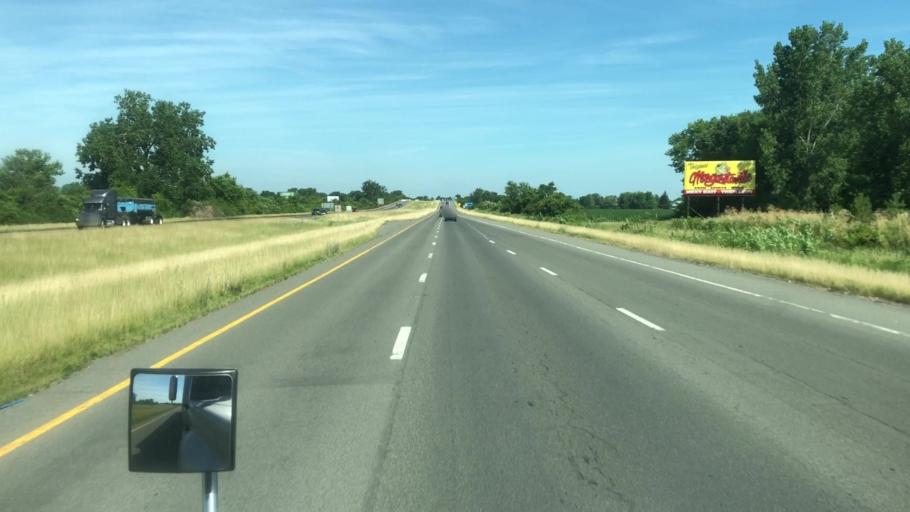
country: US
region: Ohio
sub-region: Erie County
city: Sandusky
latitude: 41.4223
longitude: -82.7631
